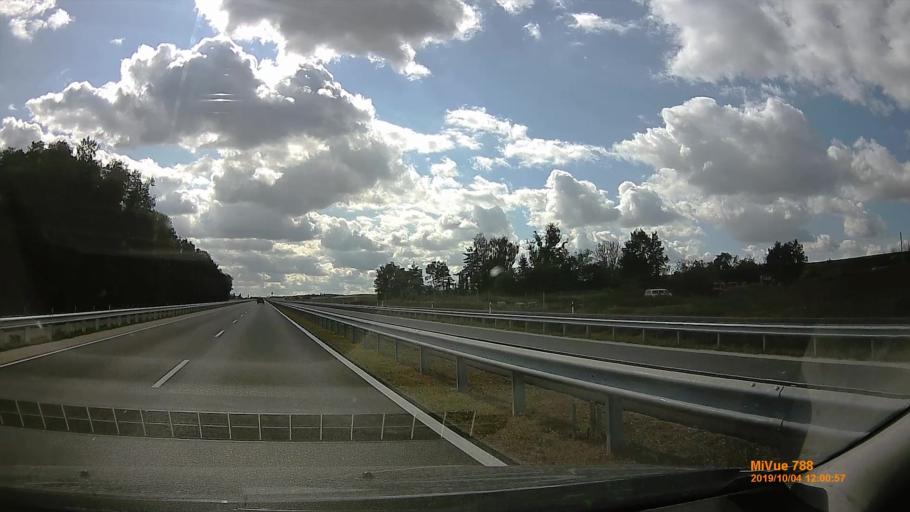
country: HU
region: Somogy
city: Karad
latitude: 46.6188
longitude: 17.7969
